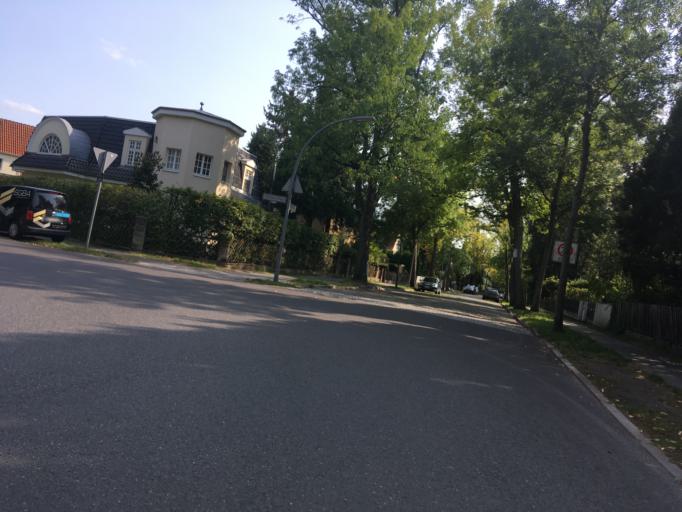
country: DE
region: Berlin
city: Frohnau
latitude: 52.6296
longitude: 13.2804
